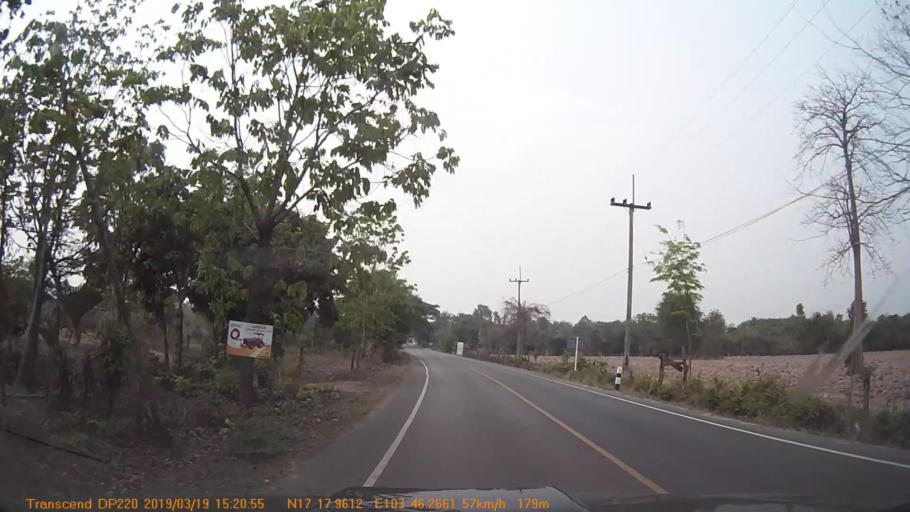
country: TH
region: Sakon Nakhon
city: Phanna Nikhom
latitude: 17.2996
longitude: 103.7710
